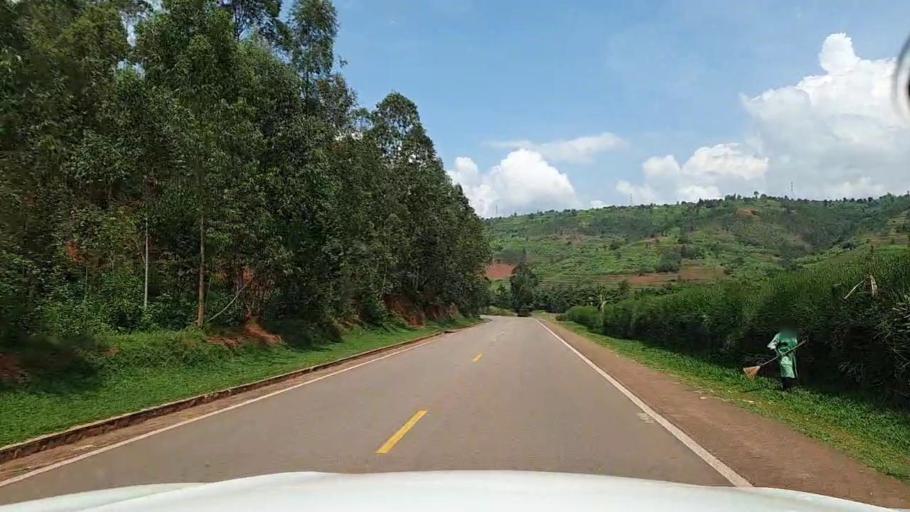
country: RW
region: Kigali
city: Kigali
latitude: -1.8464
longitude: 30.0951
